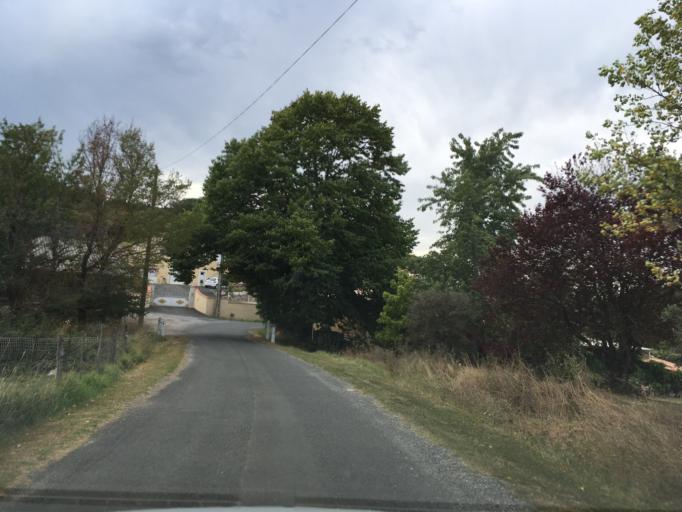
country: FR
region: Midi-Pyrenees
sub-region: Departement du Tarn
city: Lagarrigue
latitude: 43.6007
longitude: 2.2763
